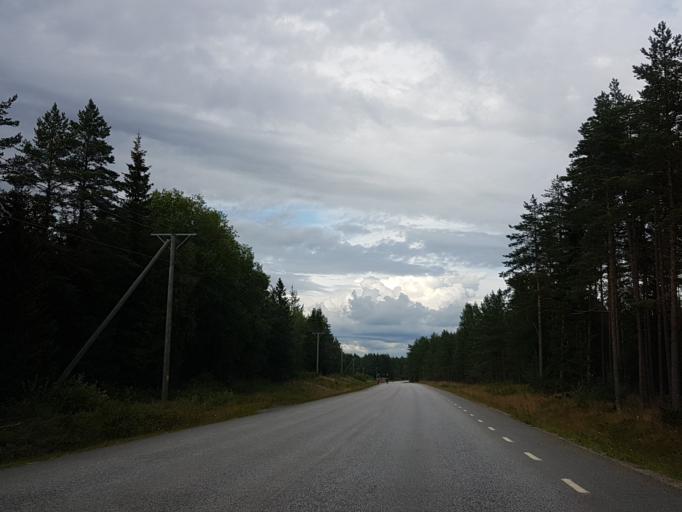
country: SE
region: Vaesterbotten
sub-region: Umea Kommun
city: Taftea
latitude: 63.8247
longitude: 20.4559
